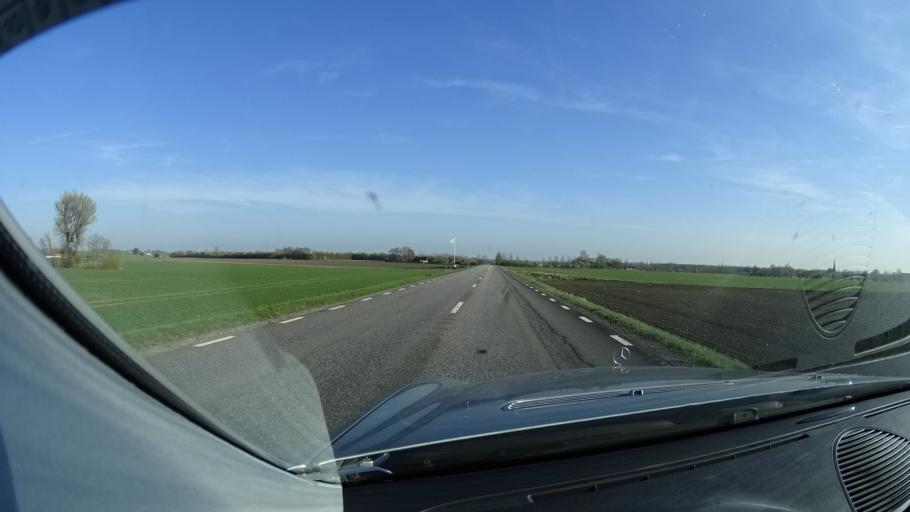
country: SE
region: Skane
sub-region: Landskrona
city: Asmundtorp
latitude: 55.9000
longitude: 12.9593
